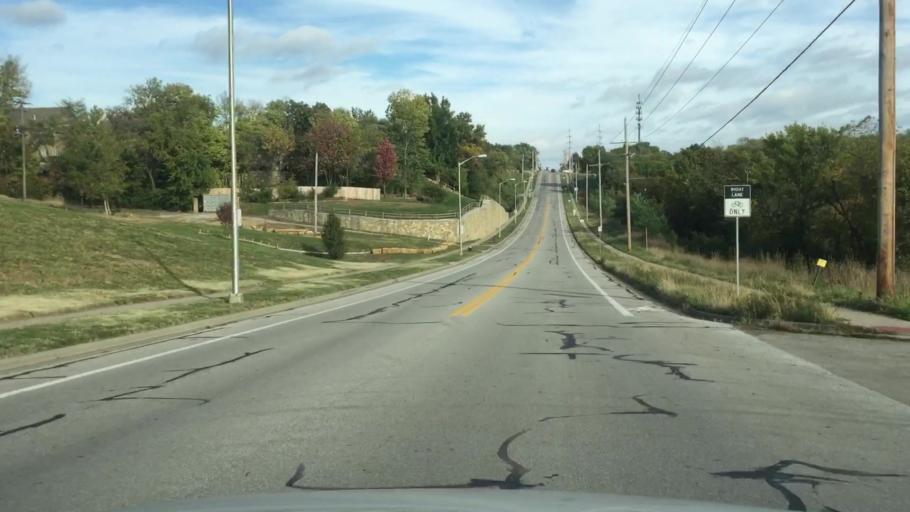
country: US
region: Kansas
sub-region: Johnson County
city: Shawnee
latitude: 39.0365
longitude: -94.7395
